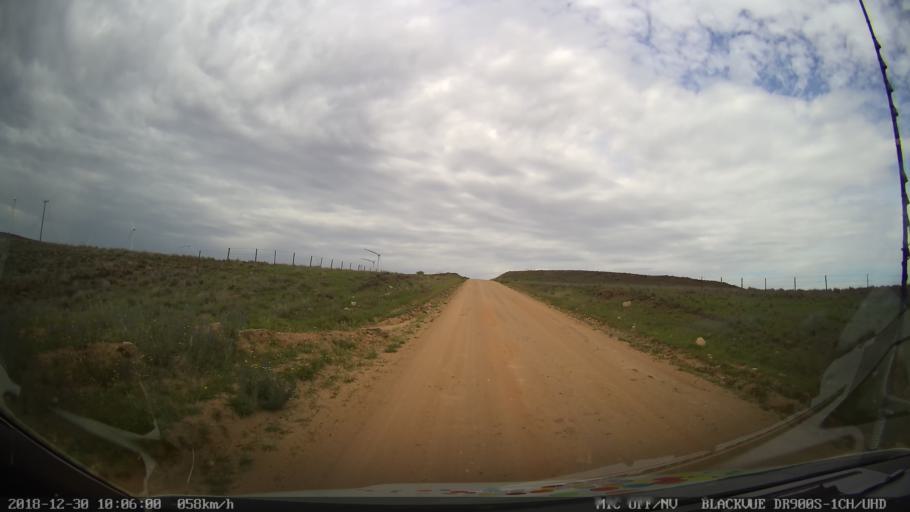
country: AU
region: New South Wales
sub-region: Cooma-Monaro
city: Cooma
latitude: -36.5311
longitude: 149.1311
